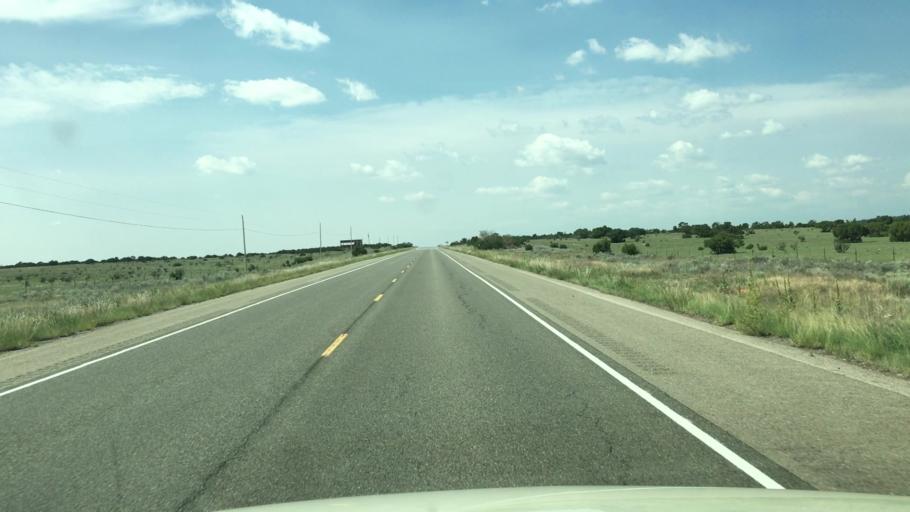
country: US
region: New Mexico
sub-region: Torrance County
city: Moriarty
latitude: 35.0378
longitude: -105.6807
